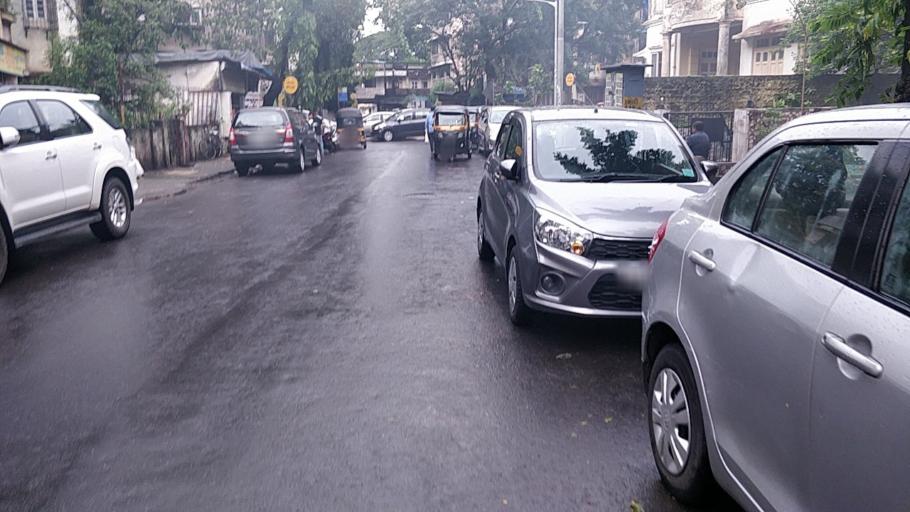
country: IN
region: Maharashtra
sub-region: Mumbai Suburban
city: Mumbai
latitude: 19.1058
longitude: 72.8429
